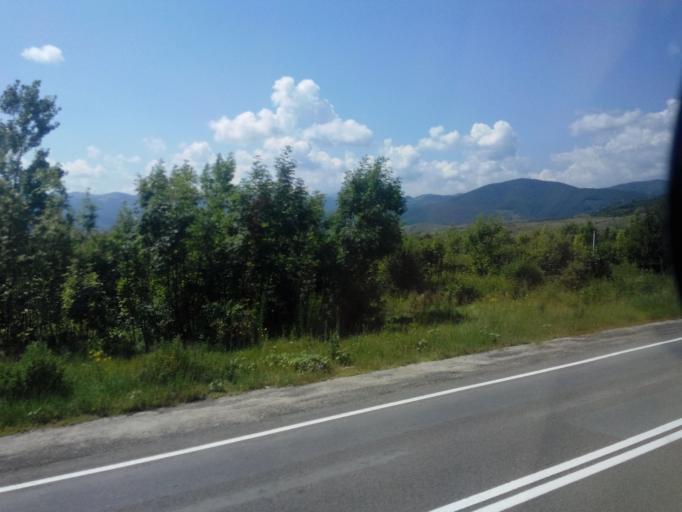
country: RO
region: Sibiu
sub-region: Comuna Orlat
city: Orlat
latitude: 45.7825
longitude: 23.9827
